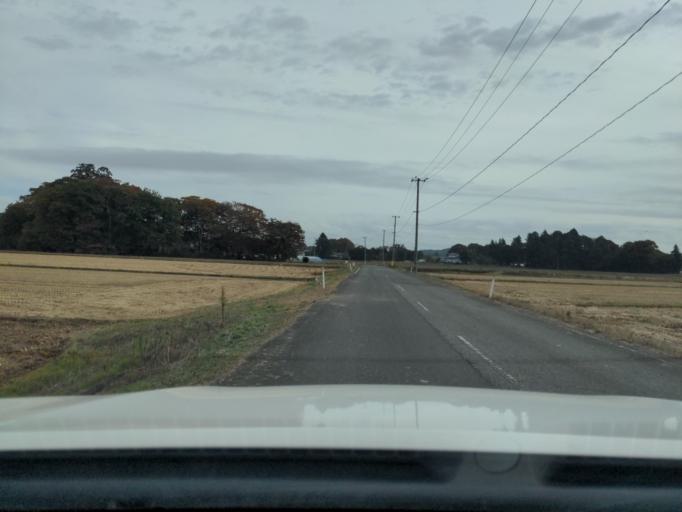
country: JP
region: Fukushima
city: Koriyama
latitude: 37.3475
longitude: 140.2802
